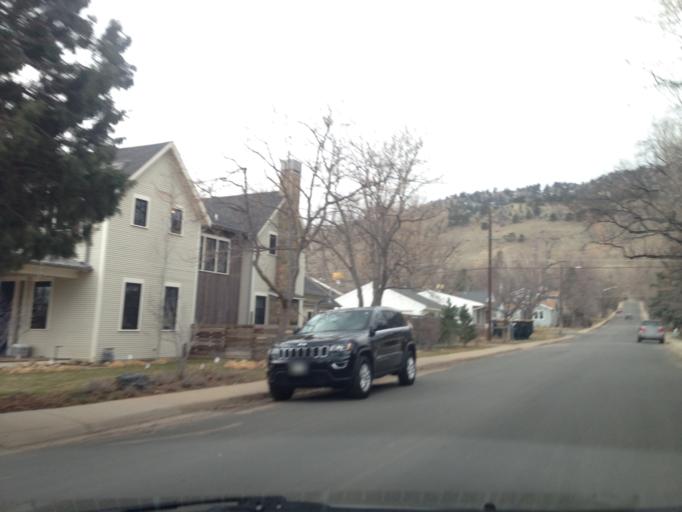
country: US
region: Colorado
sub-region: Boulder County
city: Boulder
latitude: 40.0329
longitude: -105.2869
